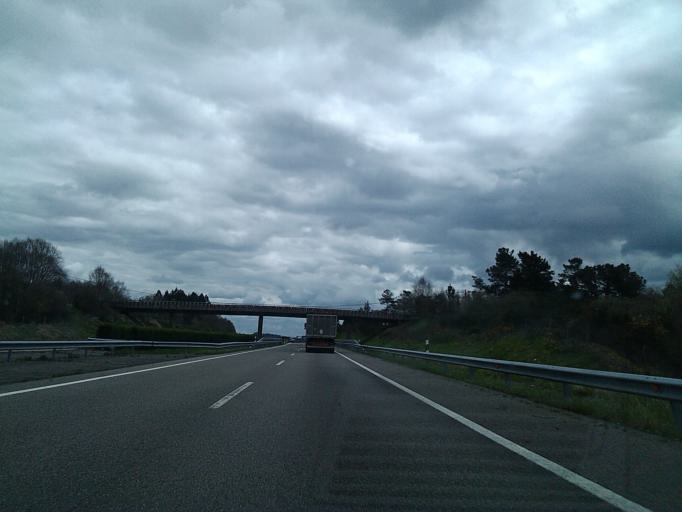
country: ES
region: Galicia
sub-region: Provincia de Lugo
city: Guitiriz
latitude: 43.1872
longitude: -7.8452
